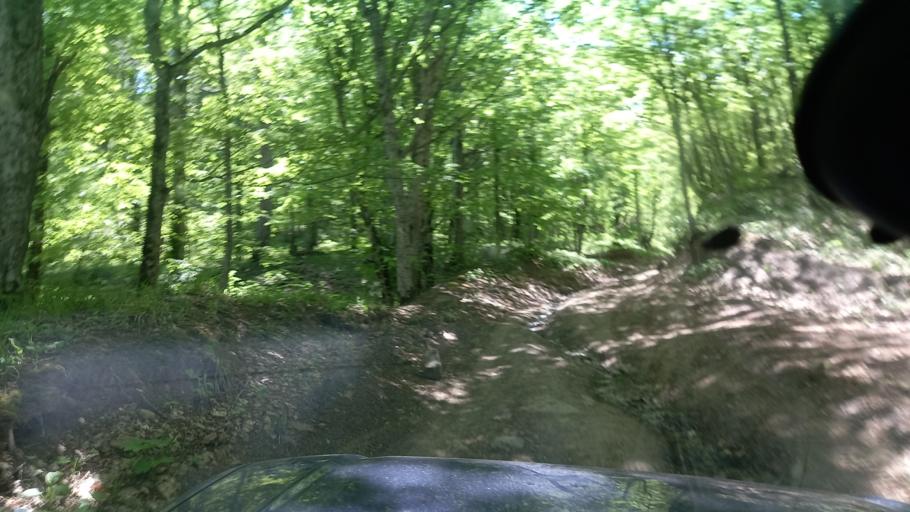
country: RU
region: Krasnodarskiy
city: Tuapse
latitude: 44.2570
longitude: 39.2845
